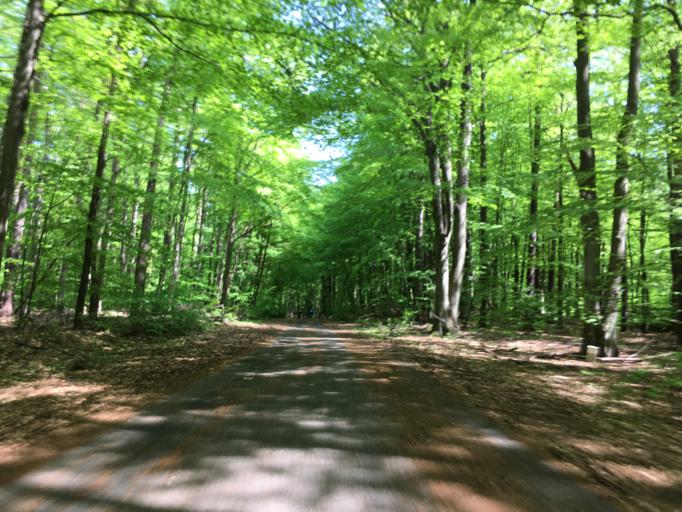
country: DE
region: Brandenburg
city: Wandlitz
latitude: 52.7318
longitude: 13.4671
